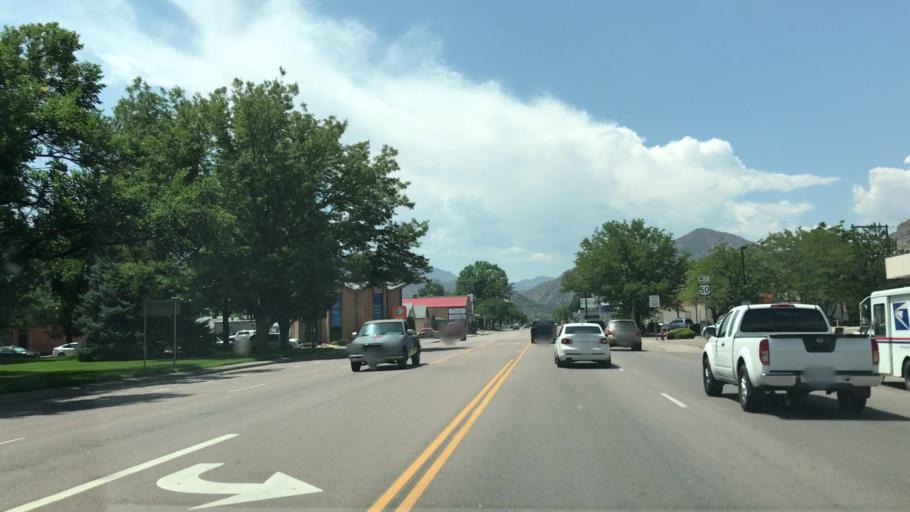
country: US
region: Colorado
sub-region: Fremont County
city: Canon City
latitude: 38.4420
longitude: -105.2354
